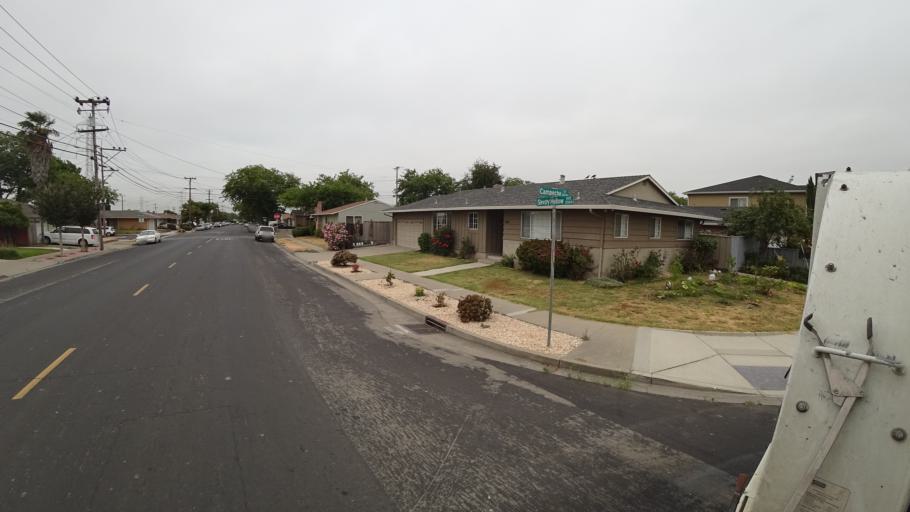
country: US
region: California
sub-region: Alameda County
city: Hayward
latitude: 37.6325
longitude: -122.1037
